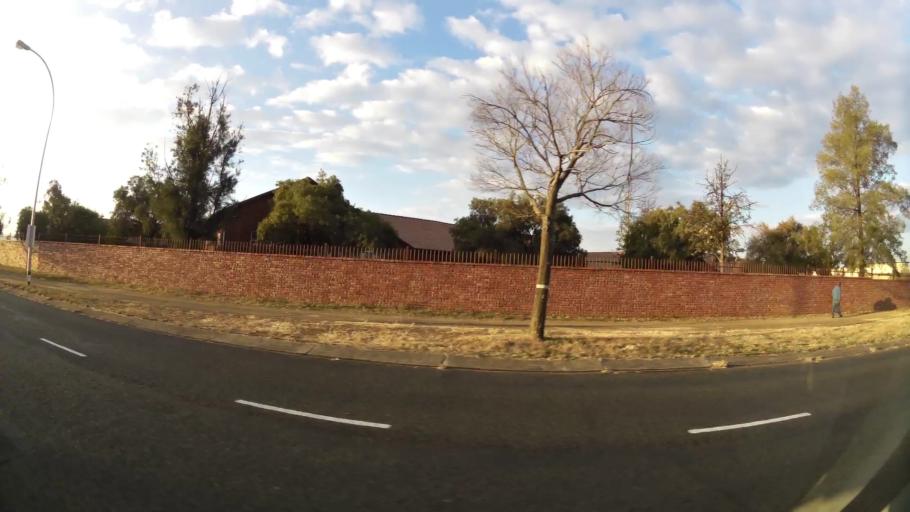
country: ZA
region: Orange Free State
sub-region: Mangaung Metropolitan Municipality
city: Bloemfontein
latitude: -29.1445
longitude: 26.1763
